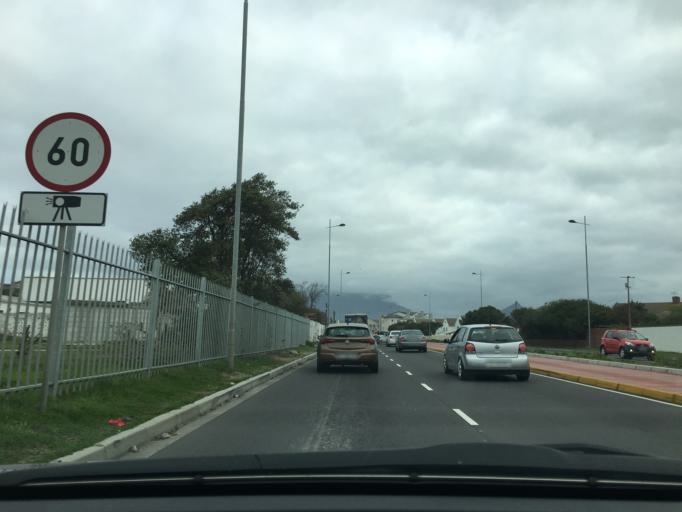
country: ZA
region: Western Cape
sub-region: City of Cape Town
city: Sunset Beach
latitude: -33.8892
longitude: 18.4879
